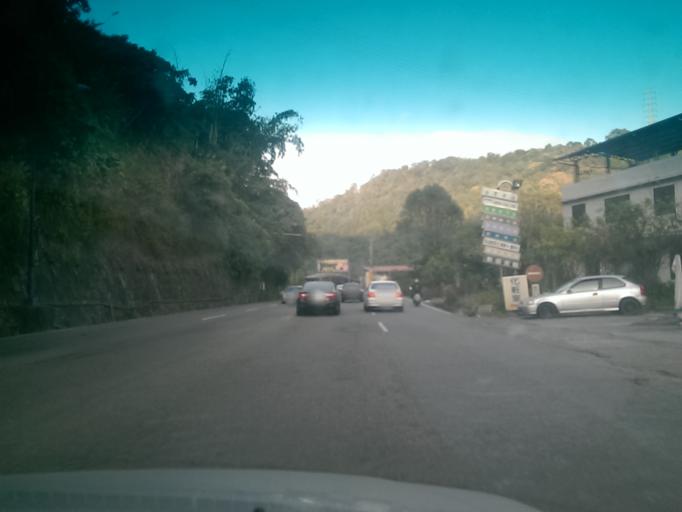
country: TW
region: Taiwan
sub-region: Nantou
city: Puli
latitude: 23.9561
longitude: 120.9417
